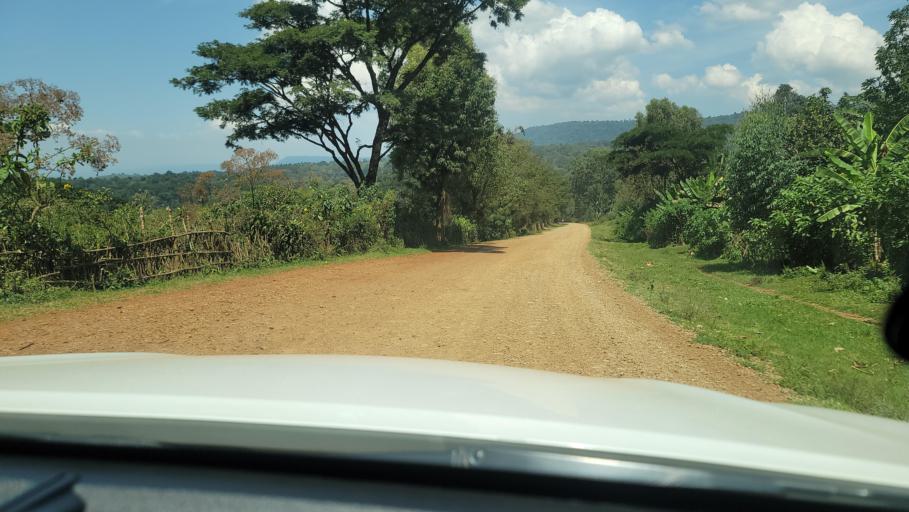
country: ET
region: Oromiya
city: Agaro
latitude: 7.7916
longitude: 36.4401
